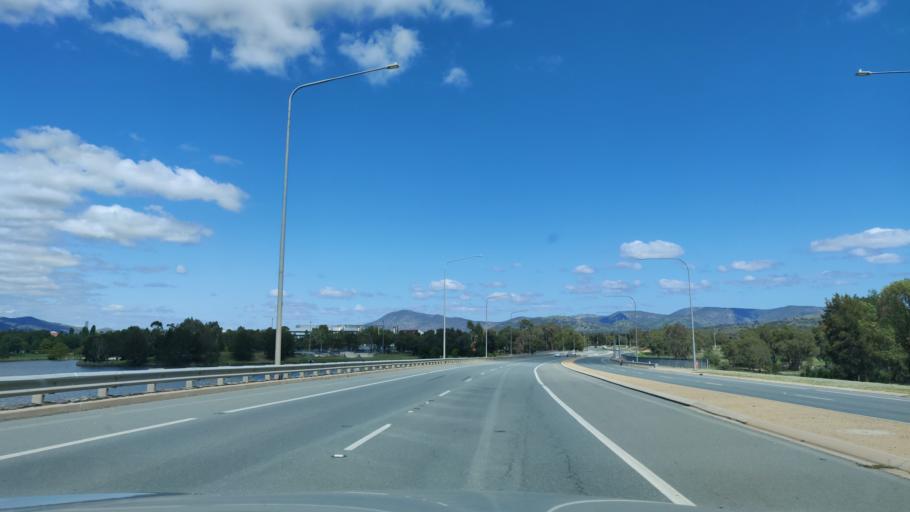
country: AU
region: Australian Capital Territory
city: Macarthur
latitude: -35.4063
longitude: 149.0643
